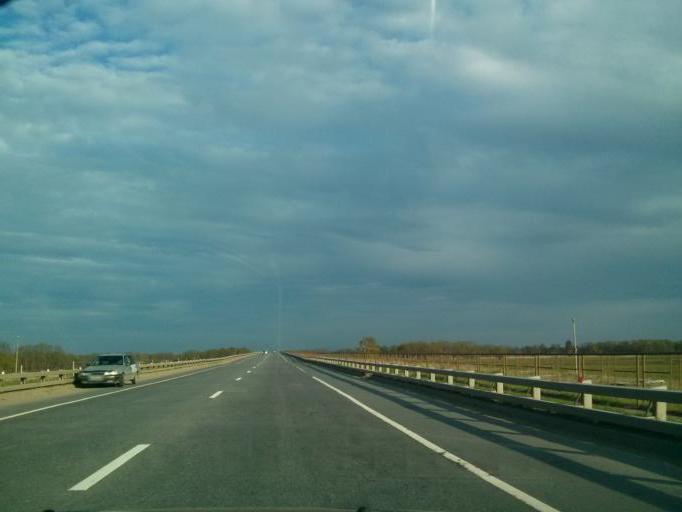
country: RU
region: Vladimir
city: Murom
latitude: 55.6091
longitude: 42.0844
